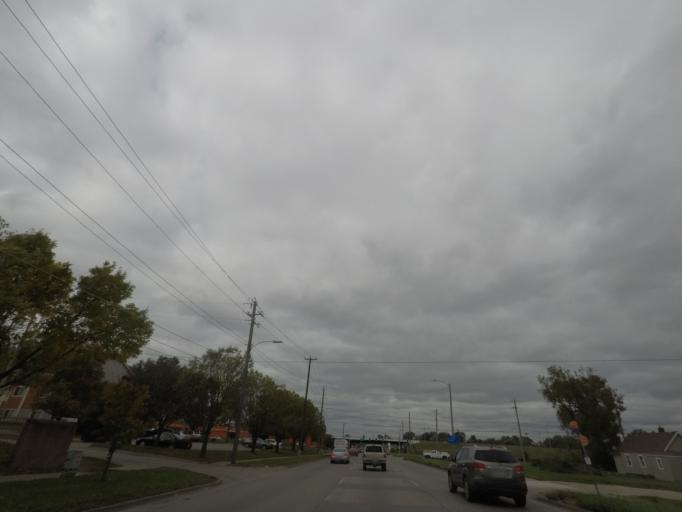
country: US
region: Iowa
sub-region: Polk County
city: Des Moines
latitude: 41.5943
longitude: -93.5954
